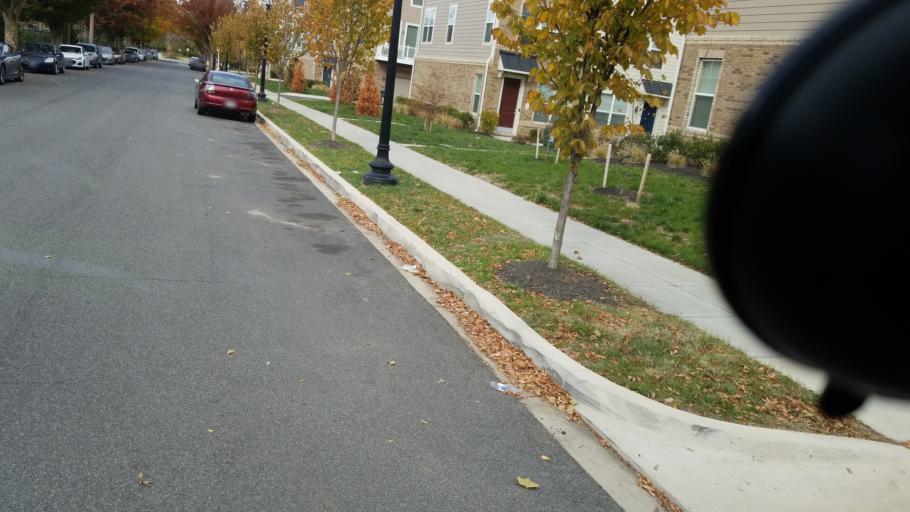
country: US
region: Maryland
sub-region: Prince George's County
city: Colmar Manor
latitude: 38.8989
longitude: -76.9514
